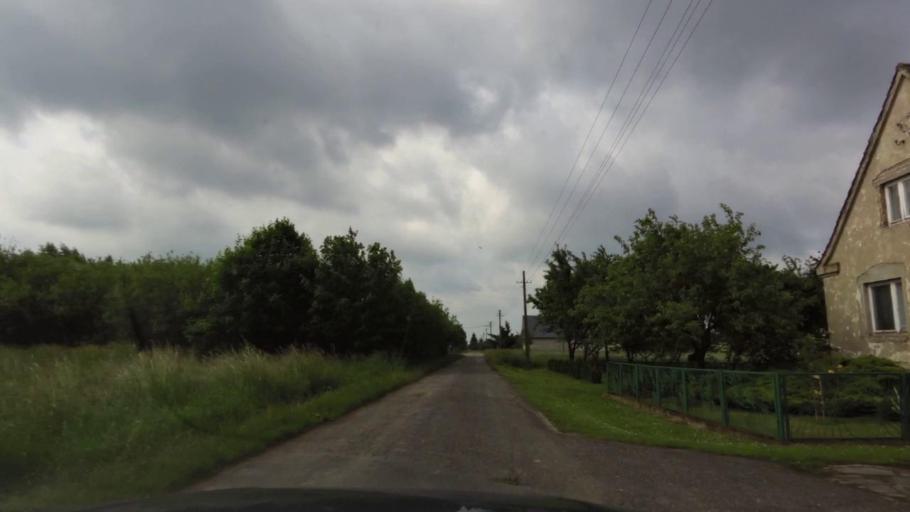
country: PL
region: West Pomeranian Voivodeship
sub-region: Powiat pyrzycki
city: Lipiany
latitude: 52.9597
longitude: 14.9546
